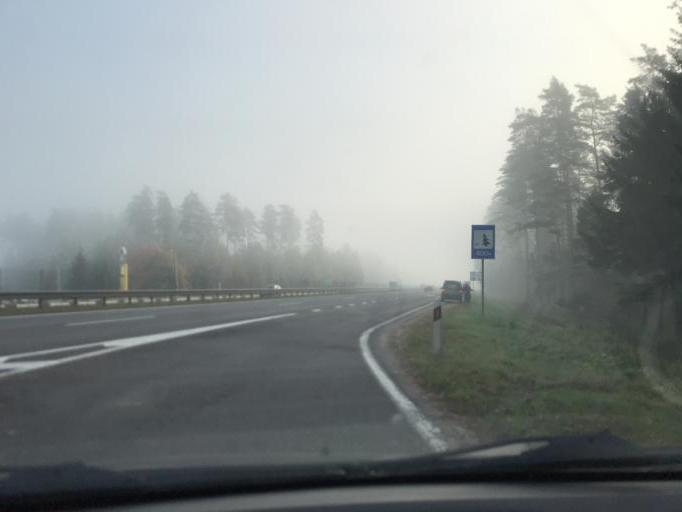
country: BY
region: Minsk
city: Pryvol'ny
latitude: 53.7977
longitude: 27.7626
